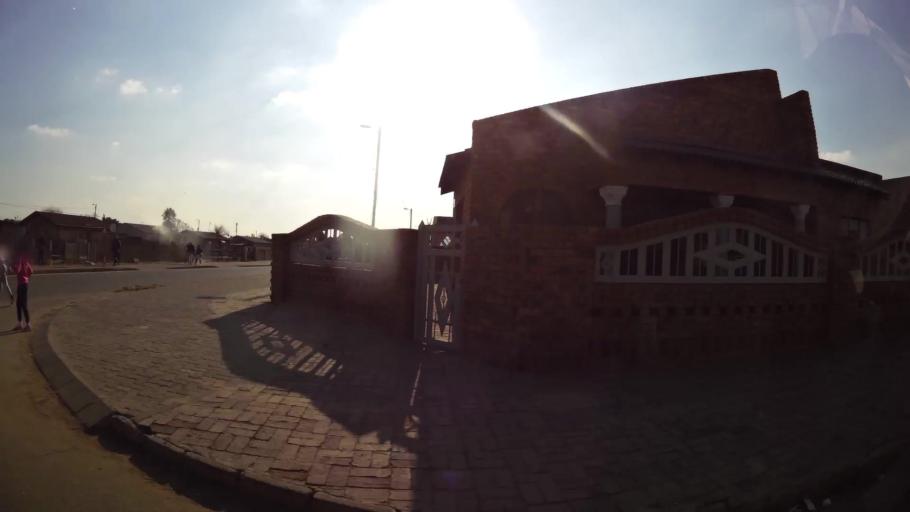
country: ZA
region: Gauteng
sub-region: Ekurhuleni Metropolitan Municipality
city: Brakpan
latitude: -26.1458
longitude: 28.4197
